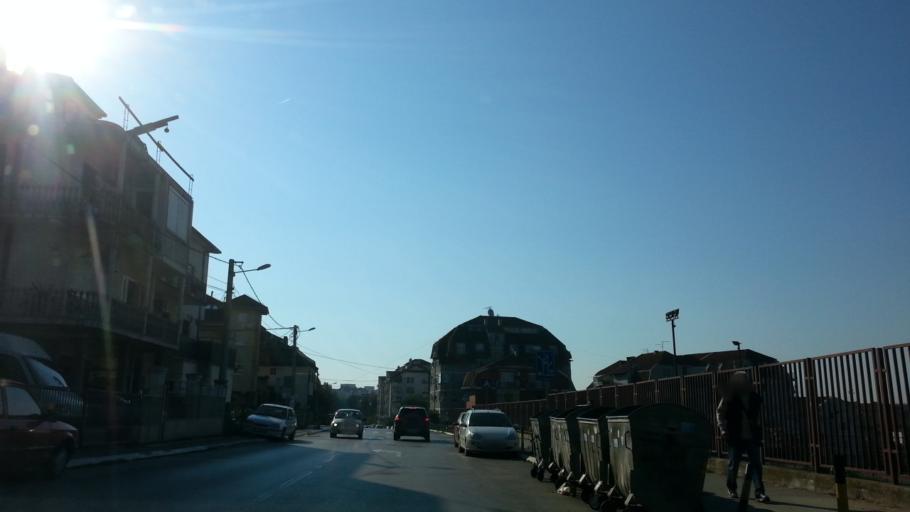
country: RS
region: Central Serbia
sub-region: Belgrade
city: Cukarica
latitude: 44.7591
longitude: 20.4201
